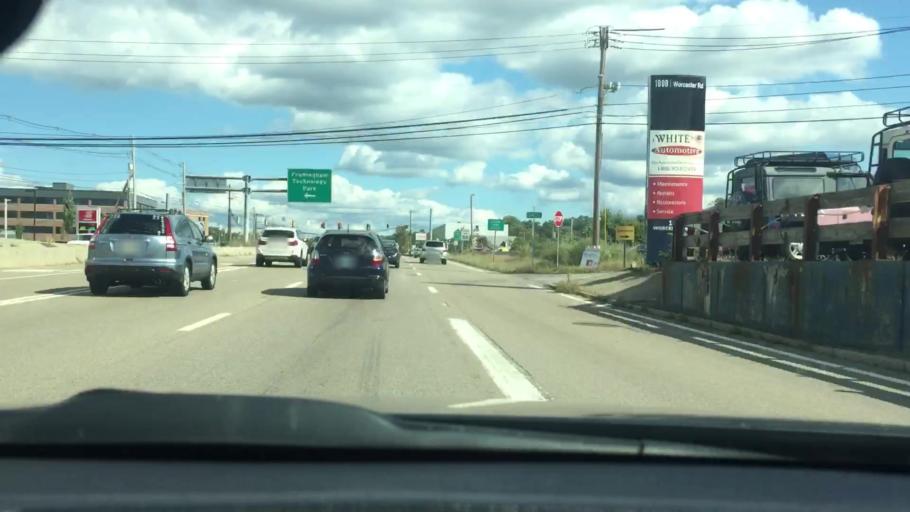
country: US
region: Massachusetts
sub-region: Worcester County
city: Southborough
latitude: 42.2950
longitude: -71.4968
